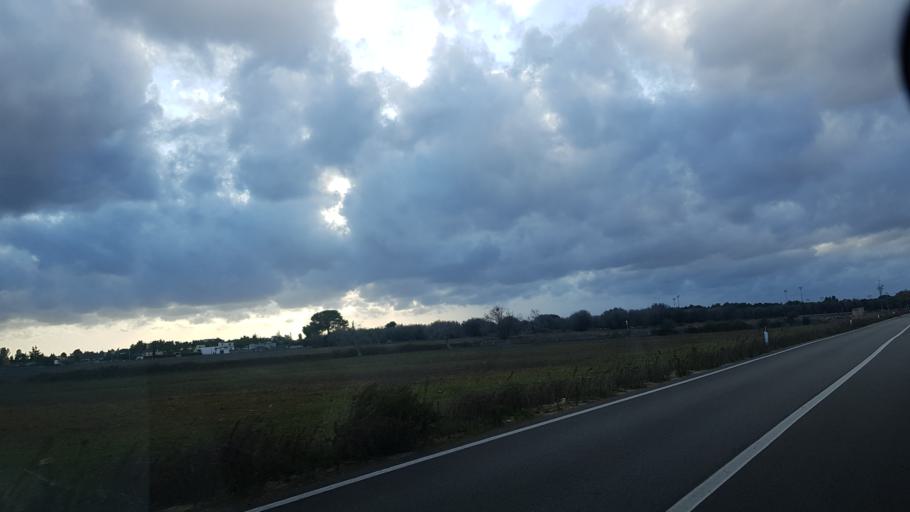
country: IT
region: Apulia
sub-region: Provincia di Brindisi
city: San Pietro Vernotico
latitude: 40.4876
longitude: 18.0143
